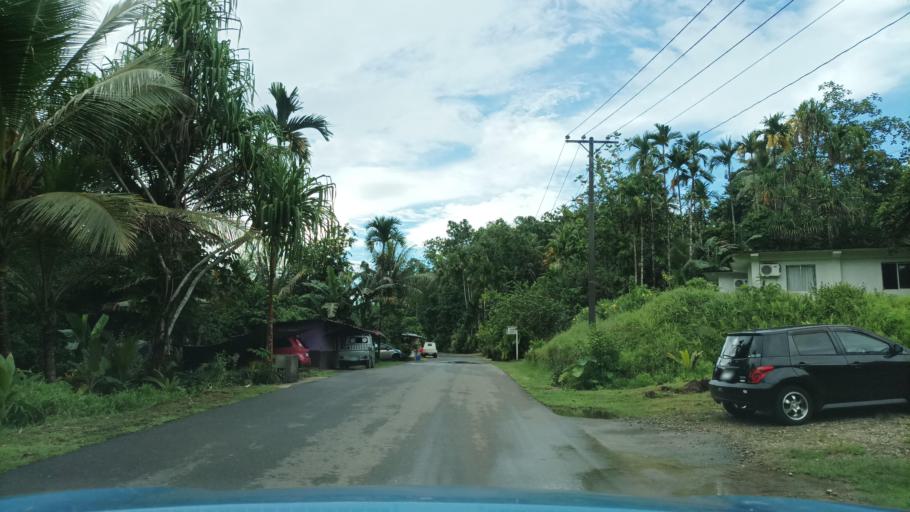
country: FM
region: Pohnpei
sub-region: Sokehs Municipality
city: Palikir - National Government Center
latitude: 6.8313
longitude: 158.1560
